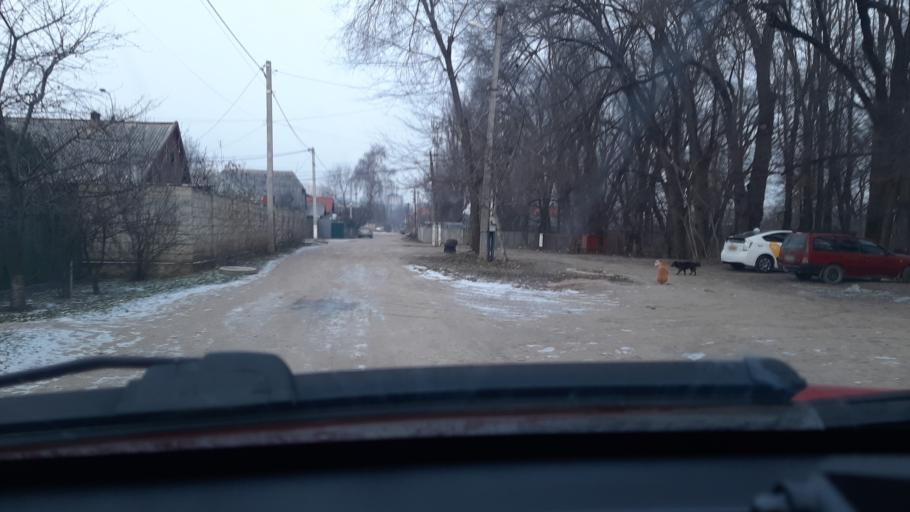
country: MD
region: Chisinau
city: Chisinau
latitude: 46.9874
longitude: 28.8931
